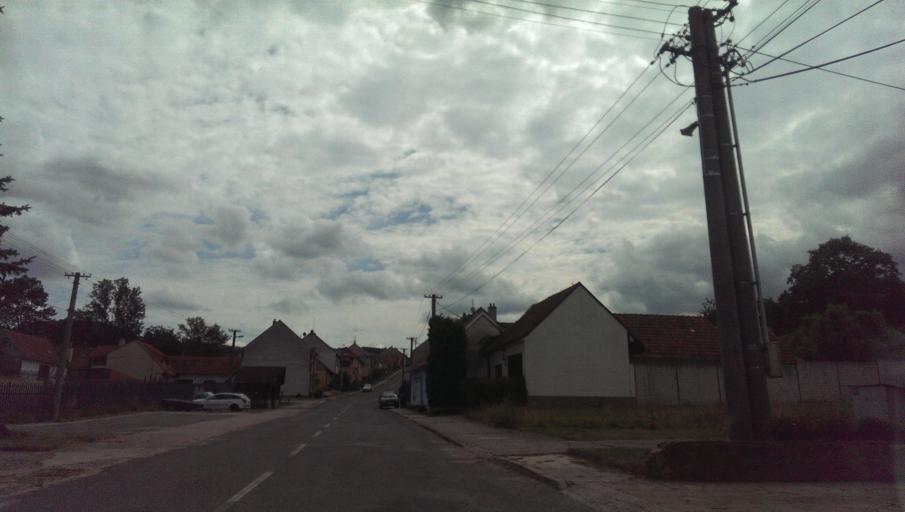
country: CZ
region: South Moravian
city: Velka nad Velickou
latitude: 48.9125
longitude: 17.5616
